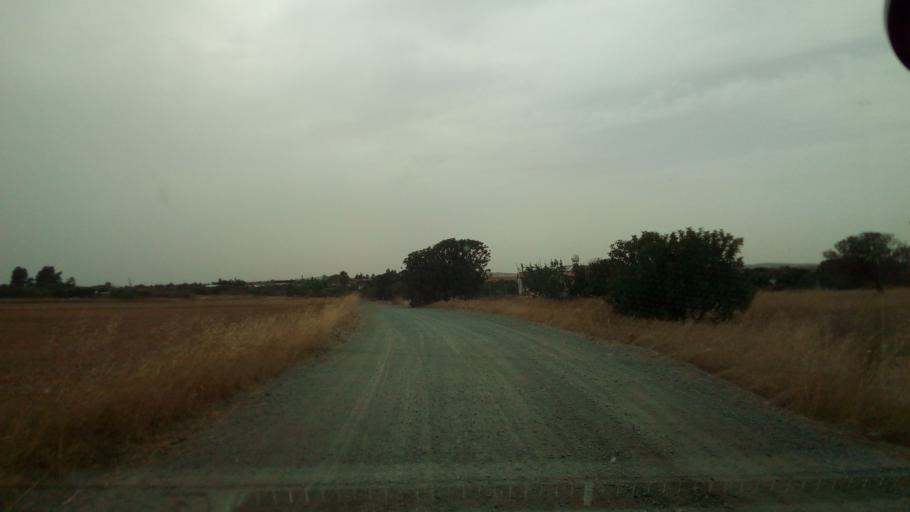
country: CY
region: Larnaka
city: Xylotymbou
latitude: 35.0200
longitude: 33.7236
